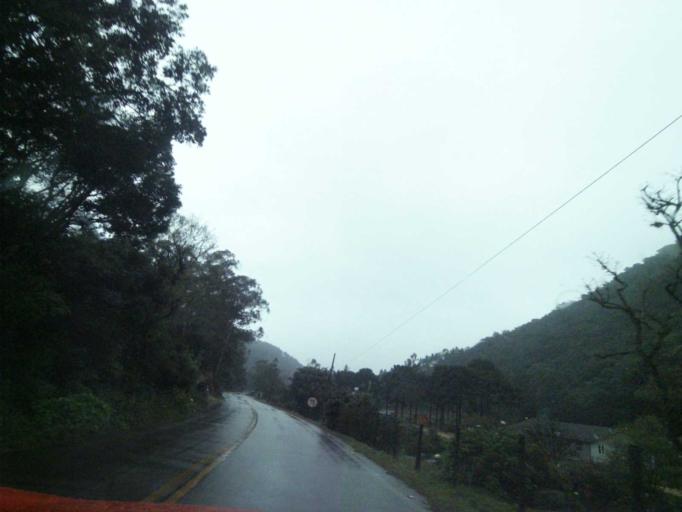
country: BR
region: Santa Catarina
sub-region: Anitapolis
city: Anitapolis
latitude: -27.8089
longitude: -49.0470
